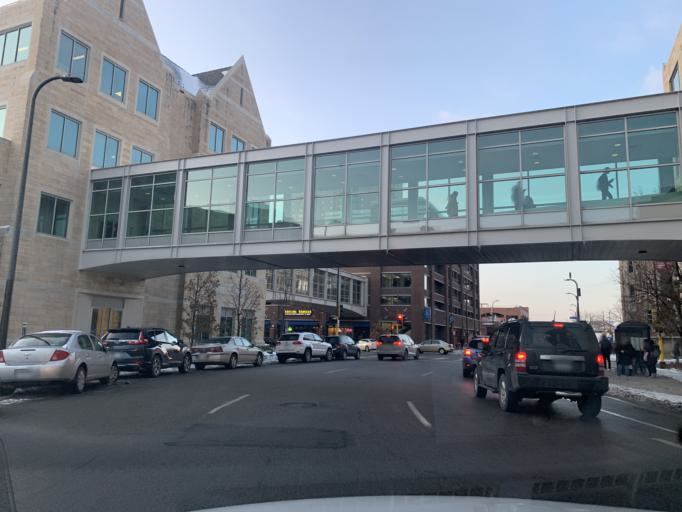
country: US
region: Minnesota
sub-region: Hennepin County
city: Minneapolis
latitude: 44.9740
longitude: -93.2779
